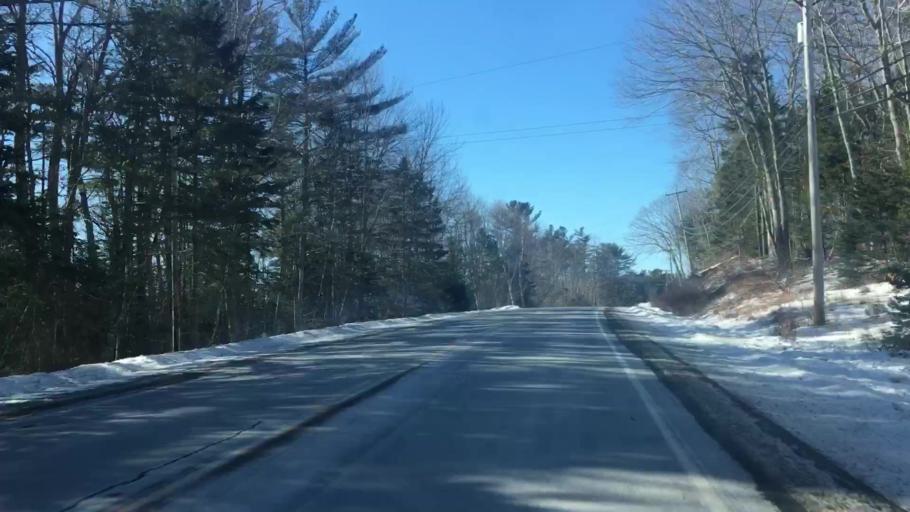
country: US
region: Maine
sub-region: Hancock County
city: Surry
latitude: 44.4947
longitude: -68.4750
